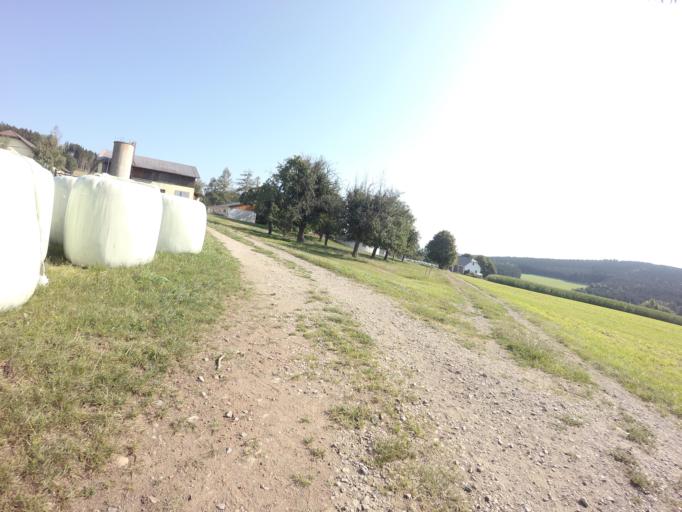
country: AT
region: Upper Austria
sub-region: Politischer Bezirk Urfahr-Umgebung
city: Bad Leonfelden
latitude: 48.5461
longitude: 14.3216
